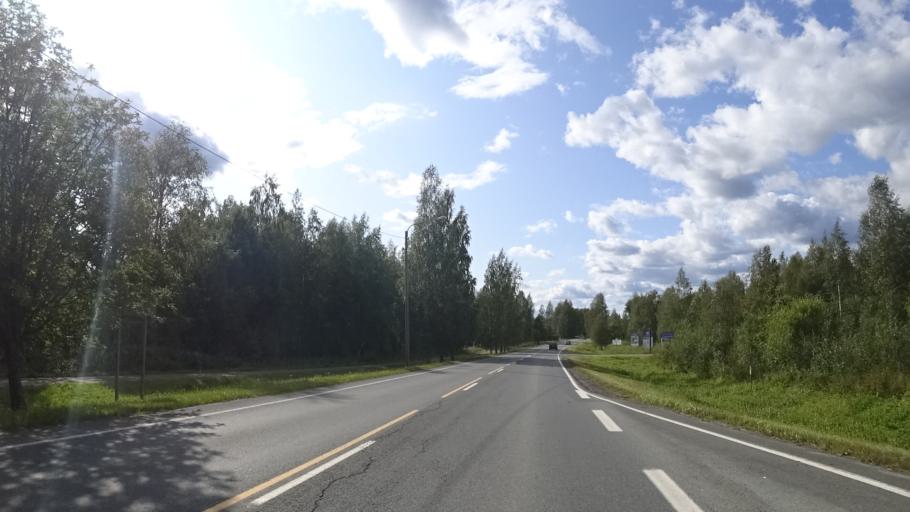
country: FI
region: North Karelia
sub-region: Keski-Karjala
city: Tohmajaervi
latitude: 62.2228
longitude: 30.3463
